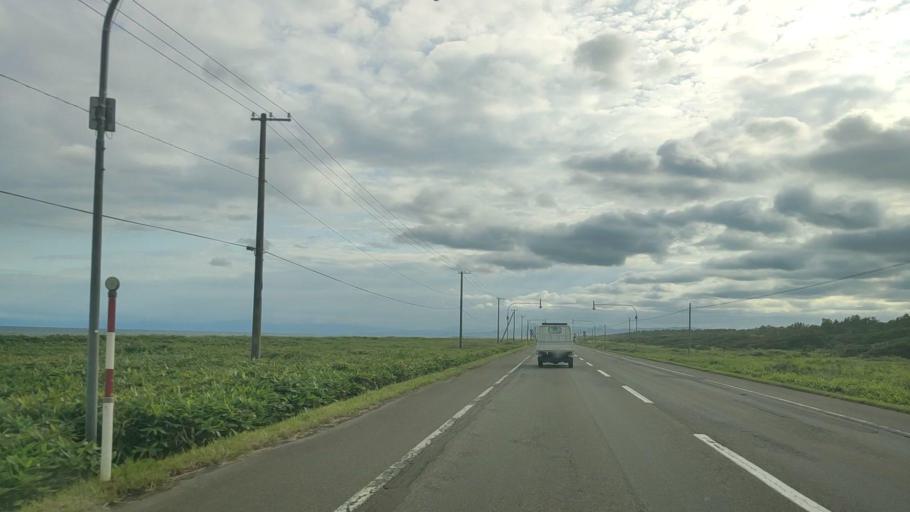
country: JP
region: Hokkaido
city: Niseko Town
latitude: 42.5691
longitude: 140.4419
